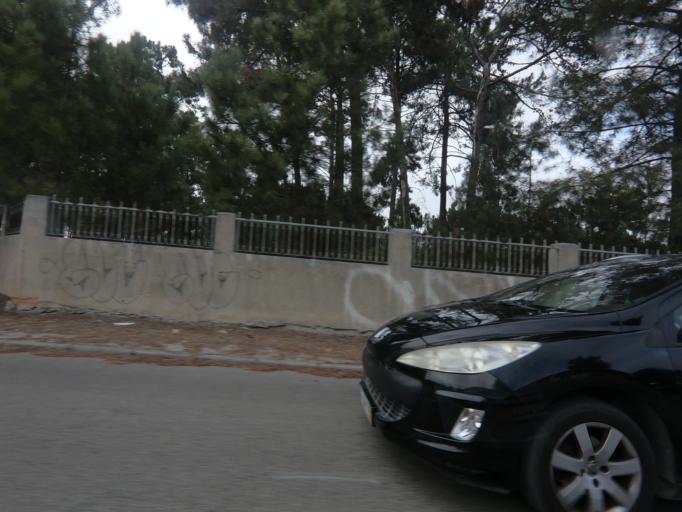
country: PT
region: Setubal
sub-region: Almada
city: Charneca
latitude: 38.5891
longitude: -9.1584
